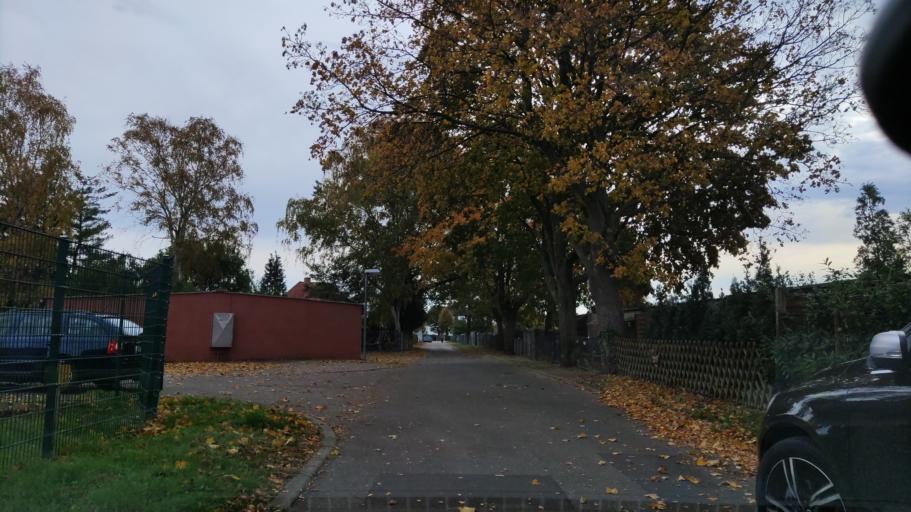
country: DE
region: Mecklenburg-Vorpommern
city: Boizenburg
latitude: 53.3743
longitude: 10.7484
